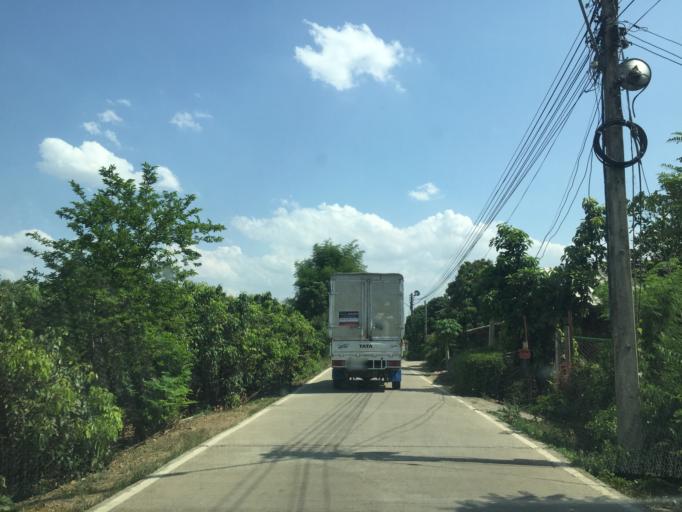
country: TH
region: Lamphun
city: Ban Thi
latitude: 18.6371
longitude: 99.0540
